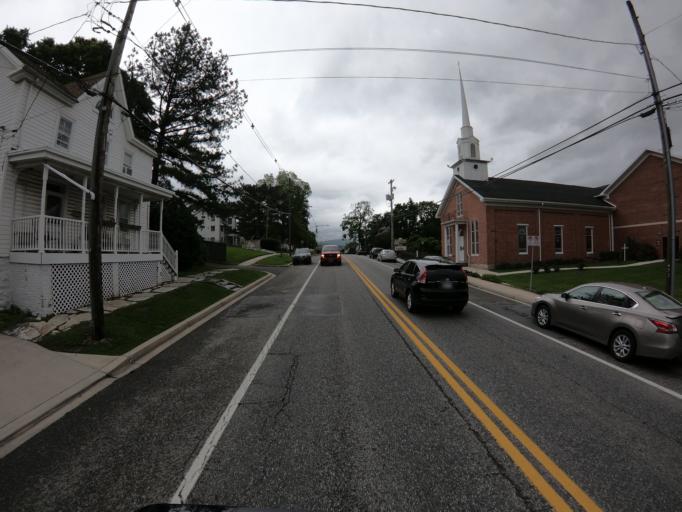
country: US
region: Maryland
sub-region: Washington County
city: Boonsboro
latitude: 39.5037
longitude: -77.6507
